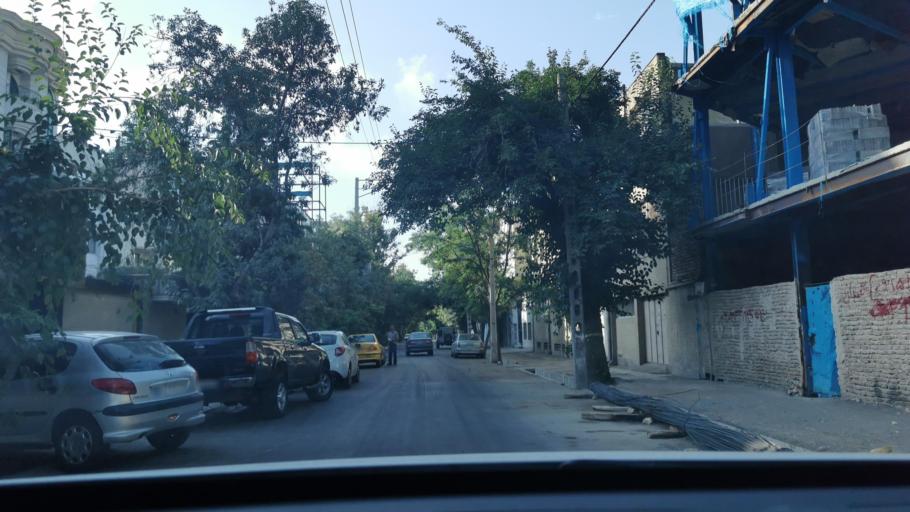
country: IR
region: Razavi Khorasan
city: Mashhad
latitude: 36.2962
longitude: 59.5830
